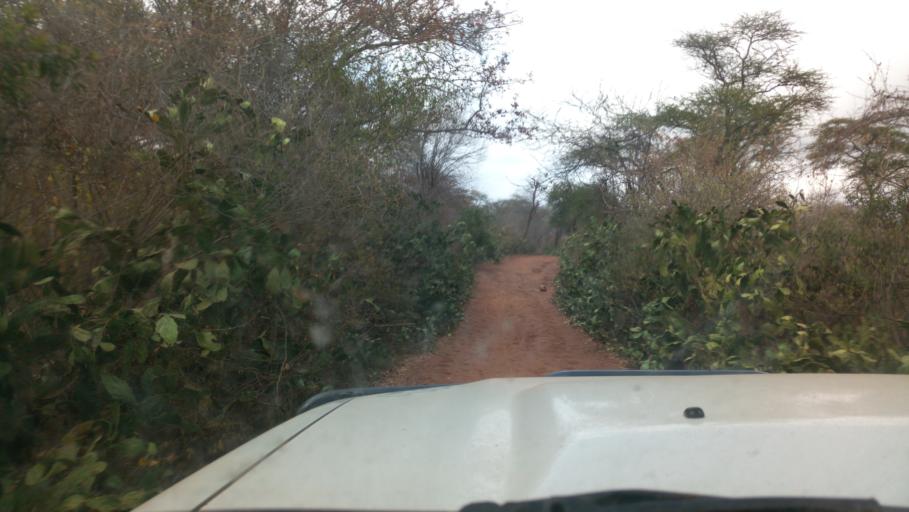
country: KE
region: Kitui
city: Kitui
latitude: -1.8660
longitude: 38.2896
